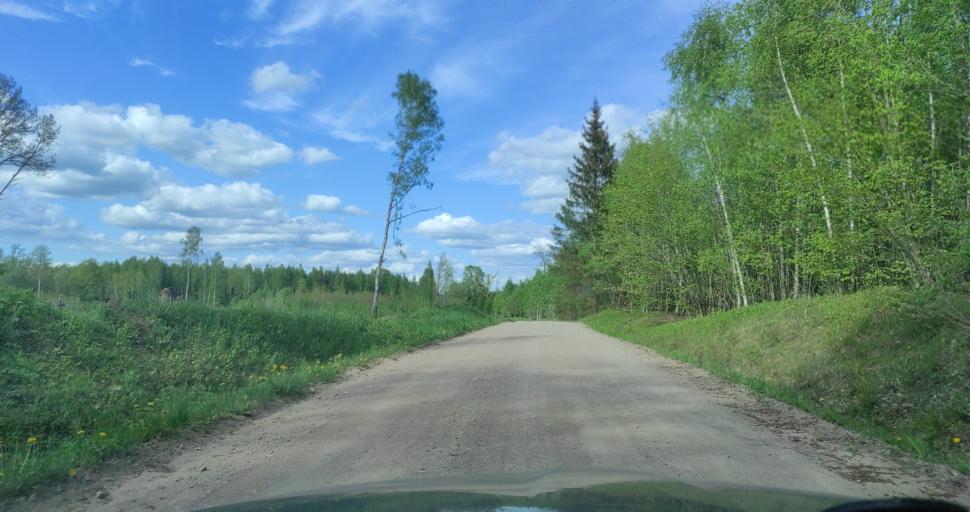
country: LV
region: Kuldigas Rajons
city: Kuldiga
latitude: 56.9445
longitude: 21.9082
